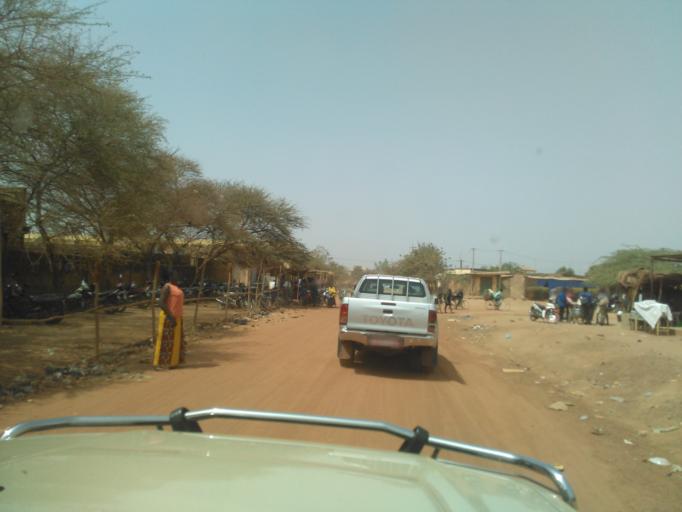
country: BF
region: Centre
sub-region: Kadiogo Province
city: Ouagadougou
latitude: 12.3815
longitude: -1.4784
